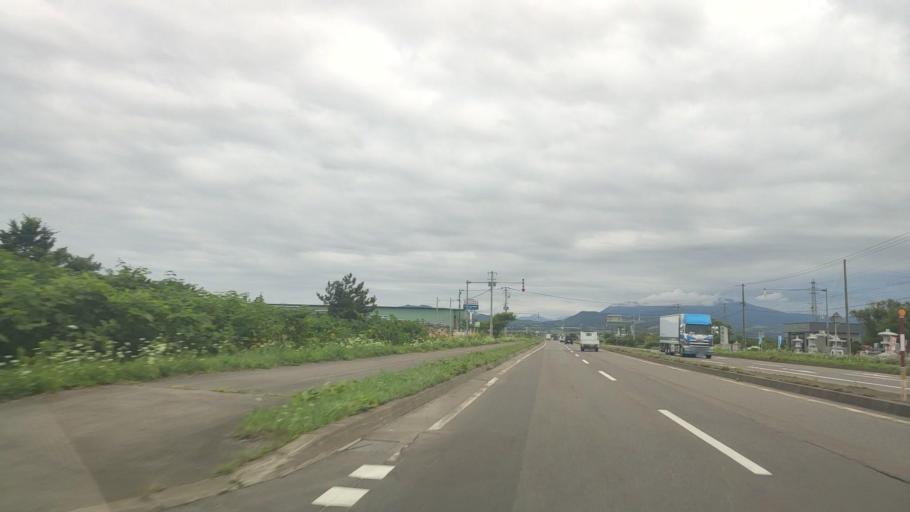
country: JP
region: Hokkaido
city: Nanae
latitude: 42.2752
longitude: 140.2723
